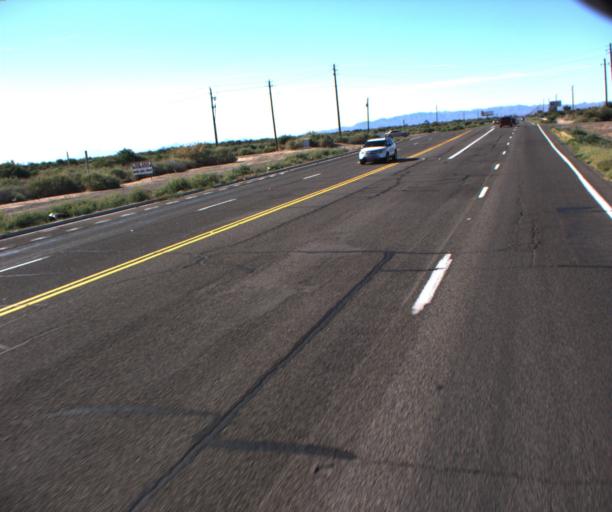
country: US
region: Arizona
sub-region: Mohave County
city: Mohave Valley
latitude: 34.9544
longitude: -114.5980
